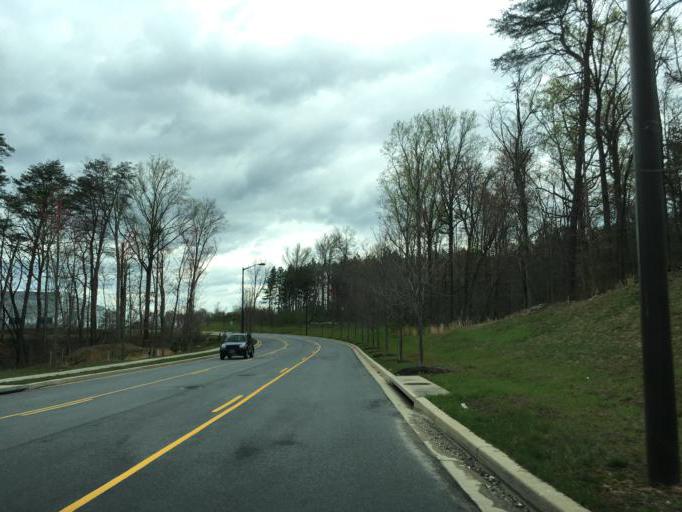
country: US
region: Maryland
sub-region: Howard County
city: Hanover
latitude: 39.1772
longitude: -76.7155
